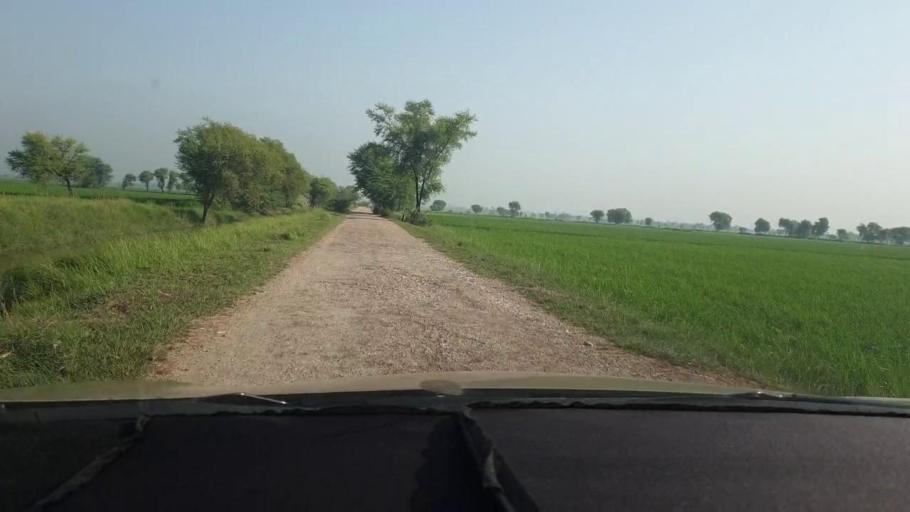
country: PK
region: Sindh
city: Kambar
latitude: 27.5845
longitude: 68.1021
